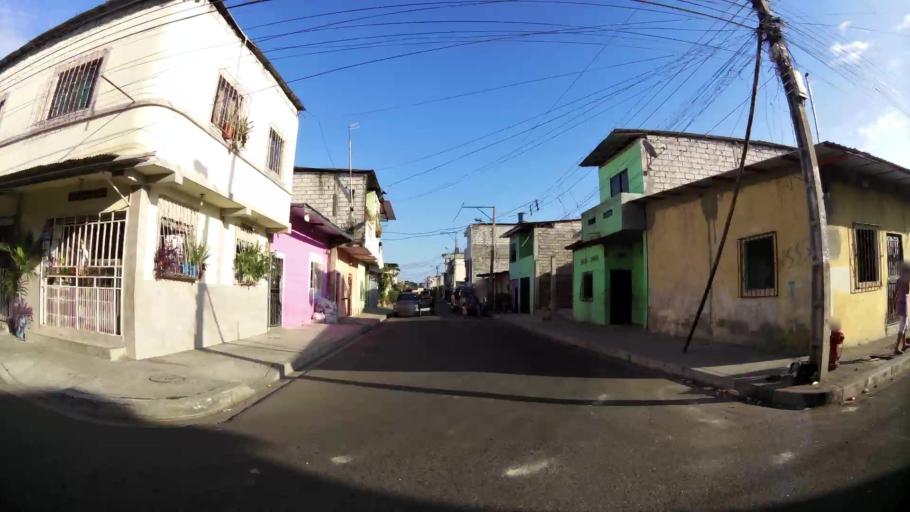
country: EC
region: Guayas
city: Guayaquil
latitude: -2.2277
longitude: -79.9120
